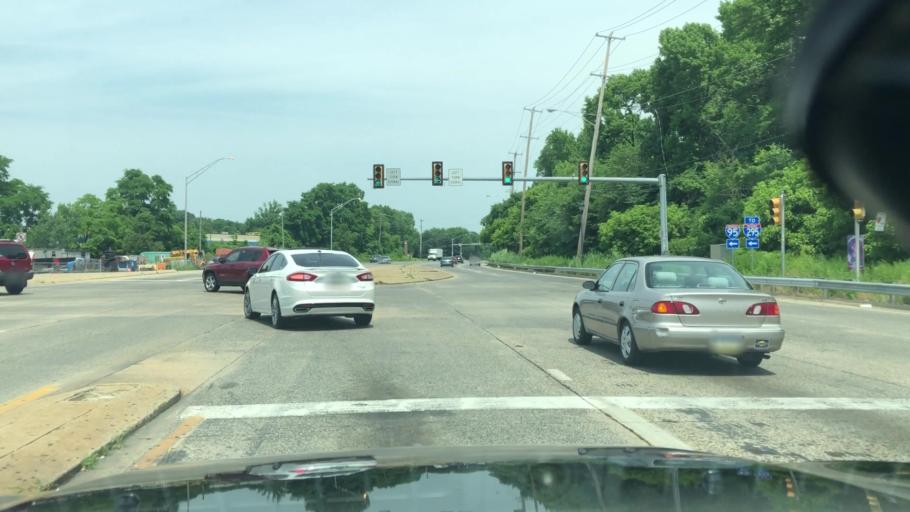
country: US
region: Pennsylvania
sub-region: Bucks County
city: Bristol
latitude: 40.1141
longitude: -74.8803
